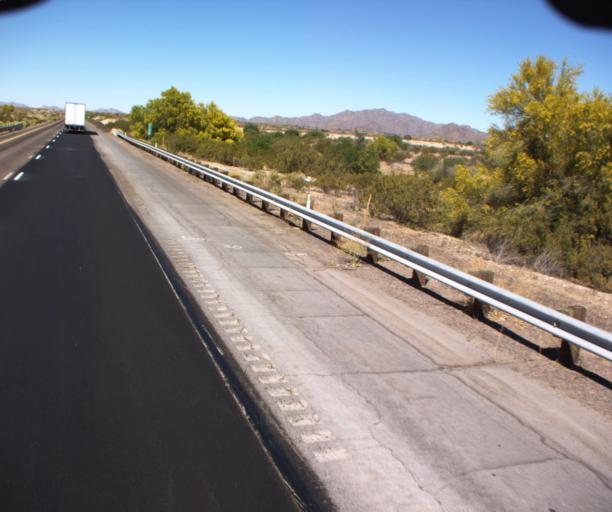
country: US
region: Arizona
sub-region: Maricopa County
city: Gila Bend
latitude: 33.0743
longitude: -112.6462
